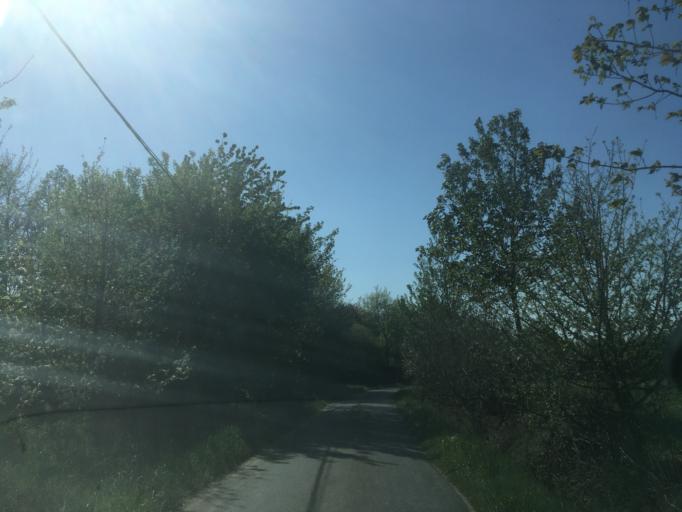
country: BE
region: Flanders
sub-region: Provincie West-Vlaanderen
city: Ardooie
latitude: 50.9586
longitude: 3.2210
